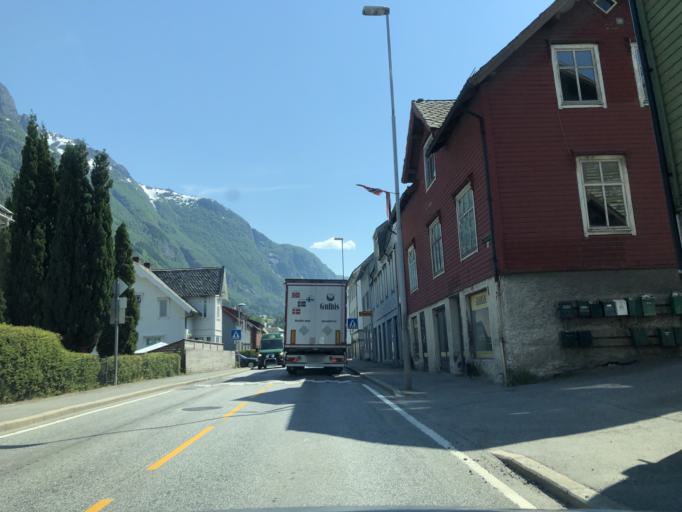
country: NO
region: Hordaland
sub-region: Odda
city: Odda
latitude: 60.0642
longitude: 6.5478
